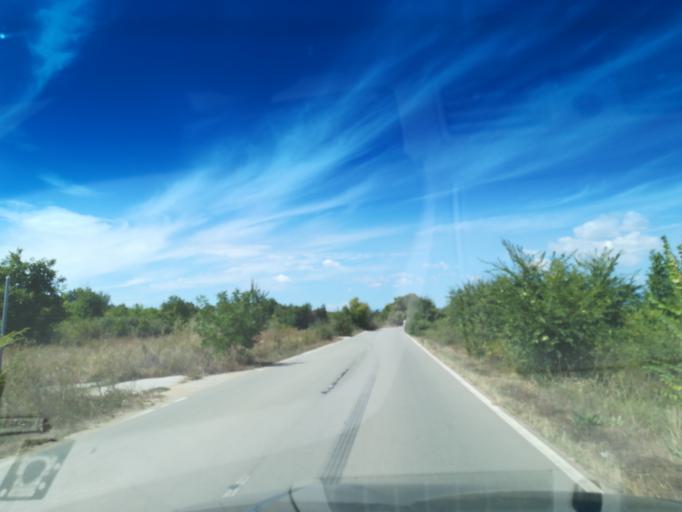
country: BG
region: Plovdiv
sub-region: Obshtina Suedinenie
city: Suedinenie
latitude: 42.3772
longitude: 24.5857
